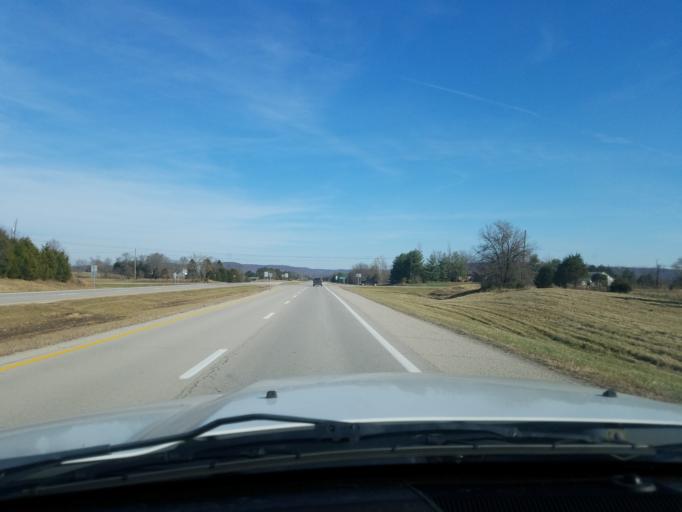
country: US
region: Ohio
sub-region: Adams County
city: Peebles
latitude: 38.9586
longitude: -83.3601
